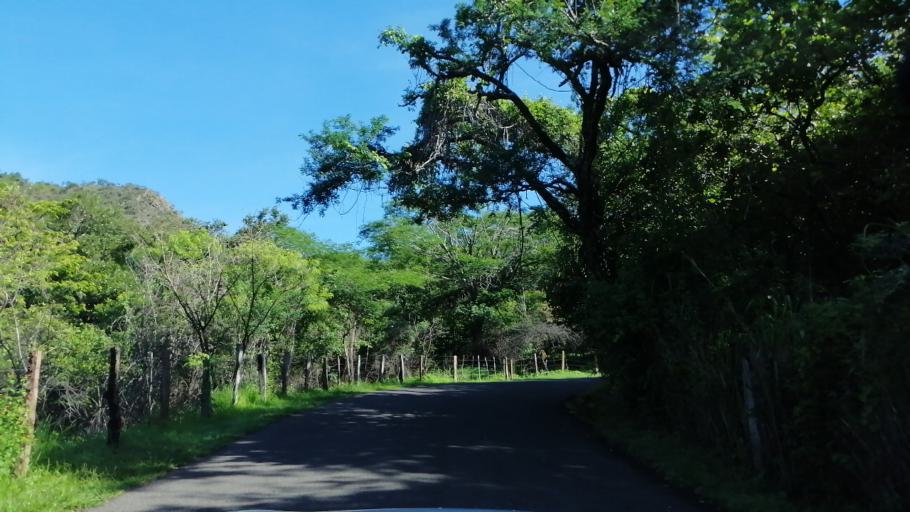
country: SV
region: Morazan
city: Corinto
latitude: 13.7979
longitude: -88.0075
